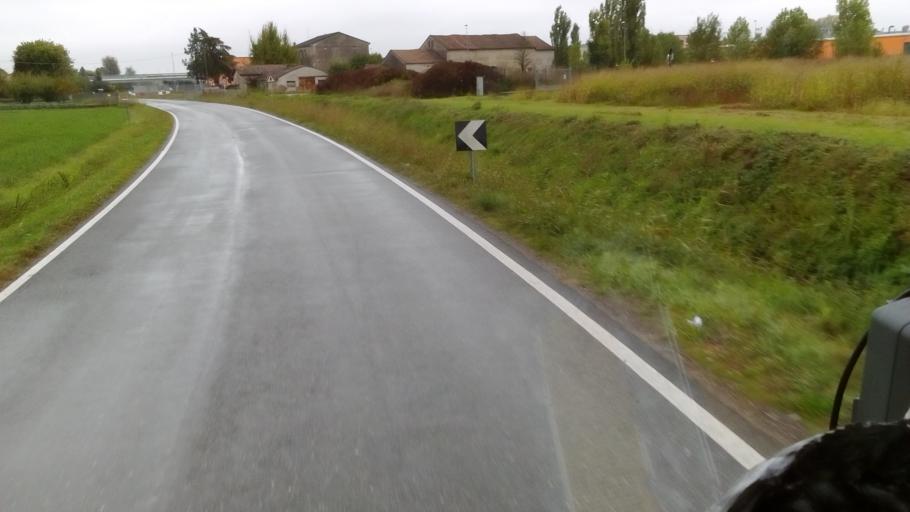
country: IT
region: Emilia-Romagna
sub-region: Provincia di Reggio Emilia
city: Luzzara
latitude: 44.9485
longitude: 10.7072
